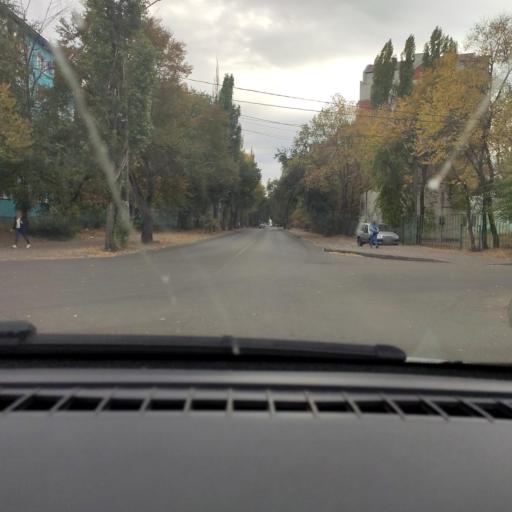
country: RU
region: Voronezj
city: Voronezh
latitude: 51.6948
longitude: 39.2636
